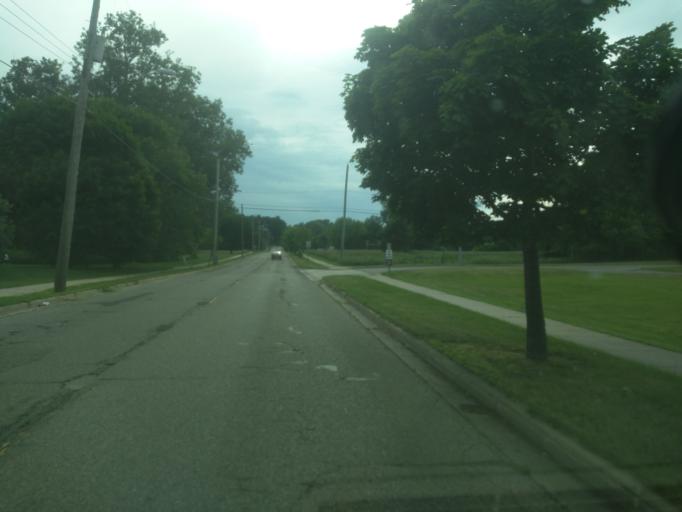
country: US
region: Michigan
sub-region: Ingham County
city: Lansing
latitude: 42.6902
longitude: -84.5570
